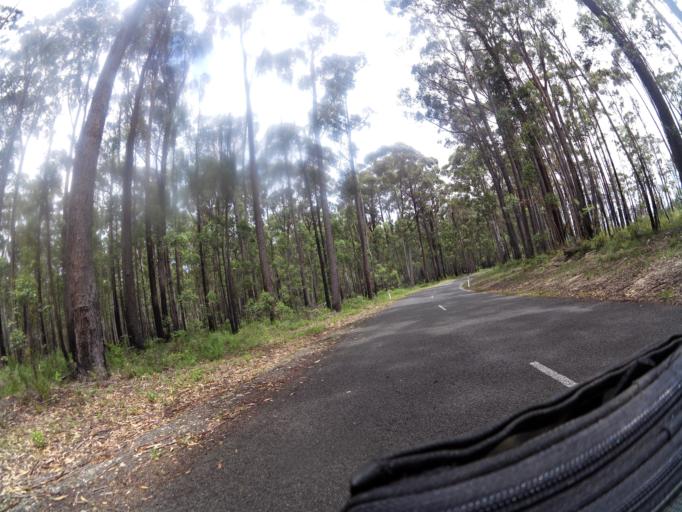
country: AU
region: Victoria
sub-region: East Gippsland
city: Lakes Entrance
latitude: -37.7035
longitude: 148.7362
